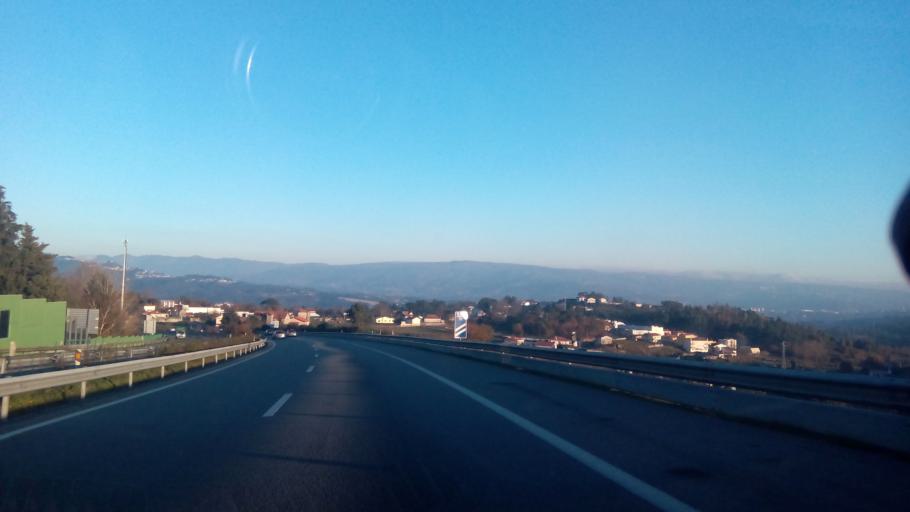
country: PT
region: Porto
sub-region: Lousada
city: Meinedo
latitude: 41.2312
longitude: -8.2153
